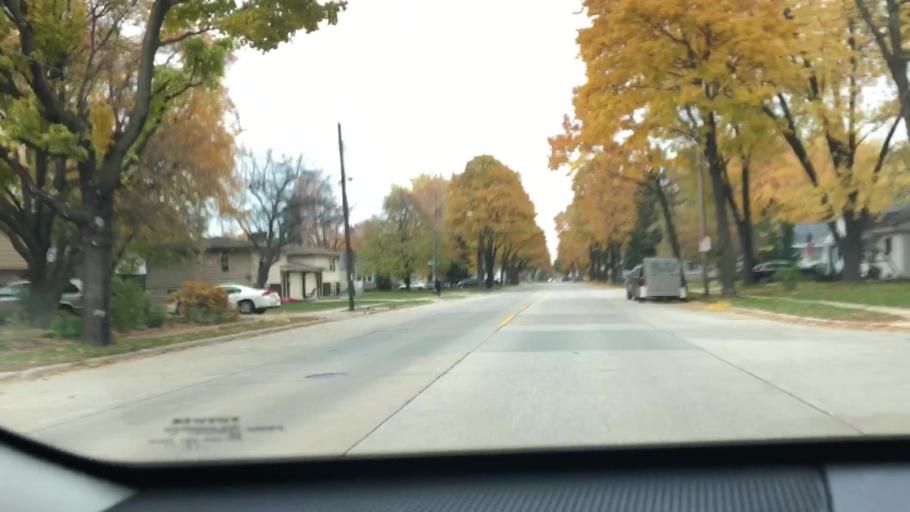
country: US
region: Wisconsin
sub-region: Brown County
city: Ashwaubenon
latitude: 44.5076
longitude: -88.0528
